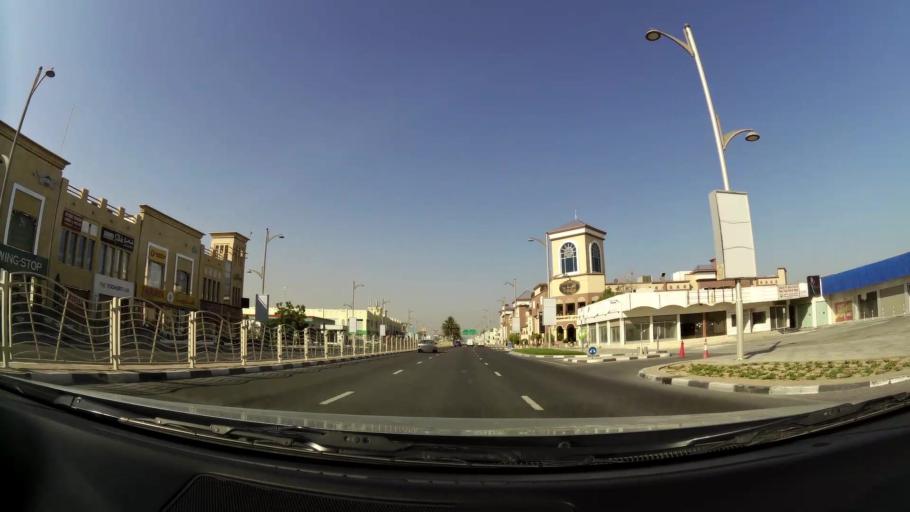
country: AE
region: Ash Shariqah
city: Sharjah
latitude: 25.2309
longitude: 55.2625
